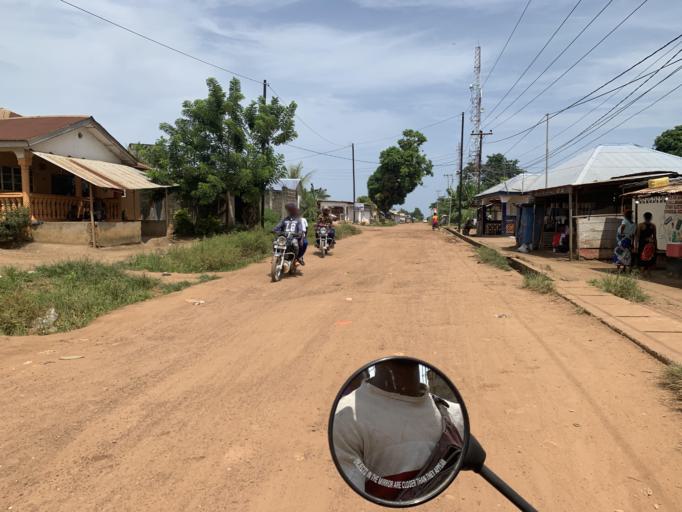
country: SL
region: Western Area
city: Hastings
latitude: 8.4072
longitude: -13.1334
